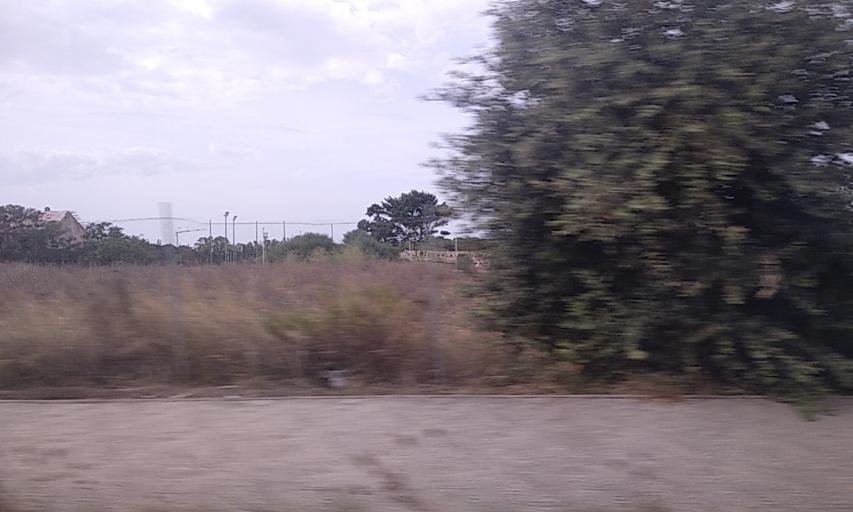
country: IT
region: Sardinia
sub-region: Provincia di Sassari
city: Alghero
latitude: 40.5854
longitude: 8.3153
